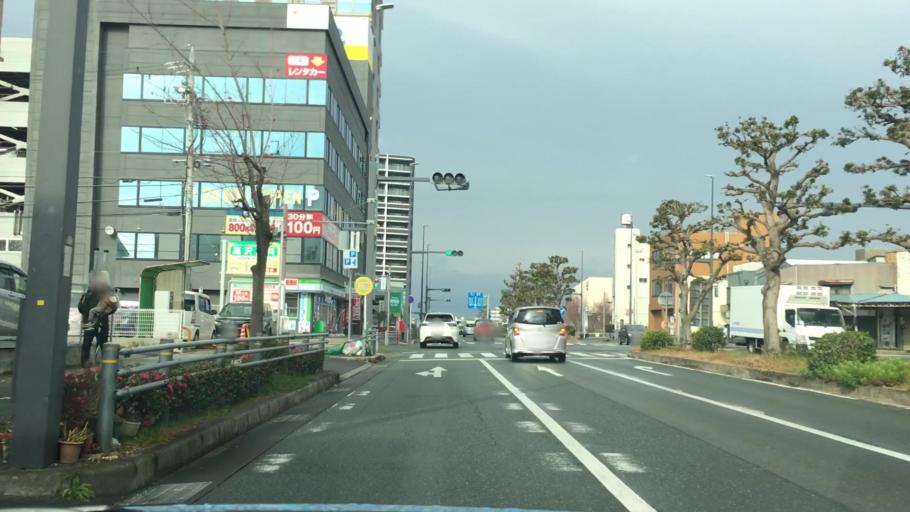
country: JP
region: Aichi
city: Toyohashi
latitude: 34.7663
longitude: 137.3829
